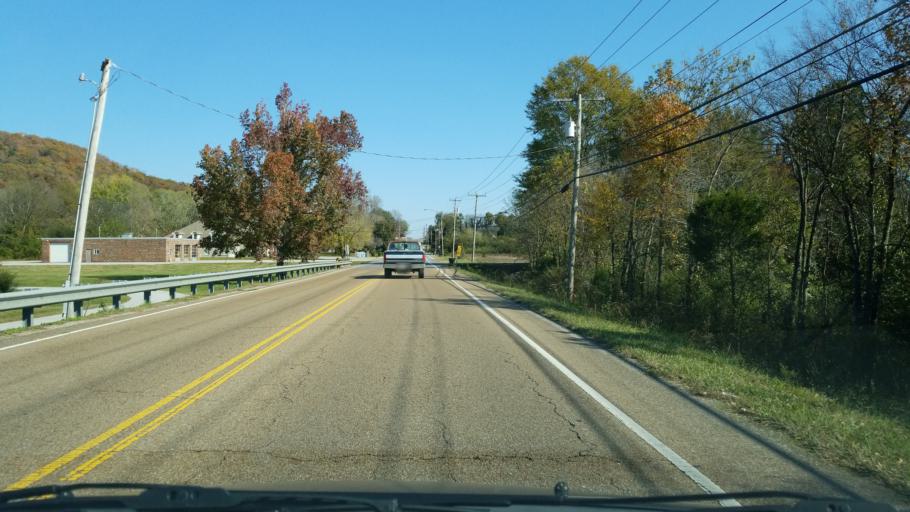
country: US
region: Tennessee
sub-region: Hamilton County
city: Soddy-Daisy
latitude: 35.2294
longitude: -85.2105
